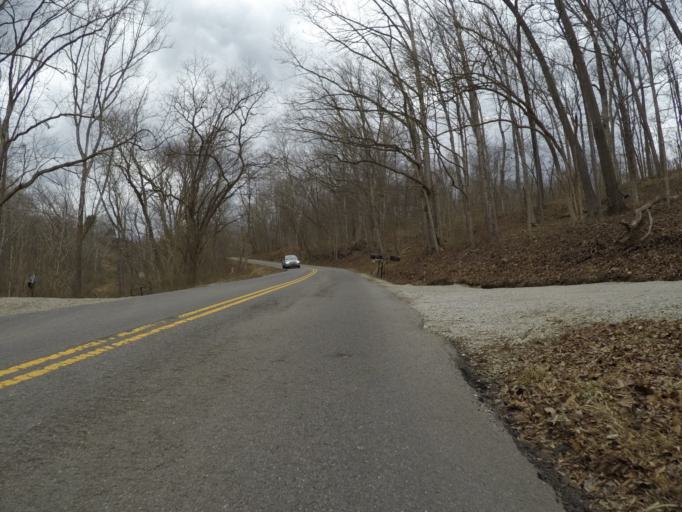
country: US
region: Ohio
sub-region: Lawrence County
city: Burlington
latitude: 38.4297
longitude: -82.5251
